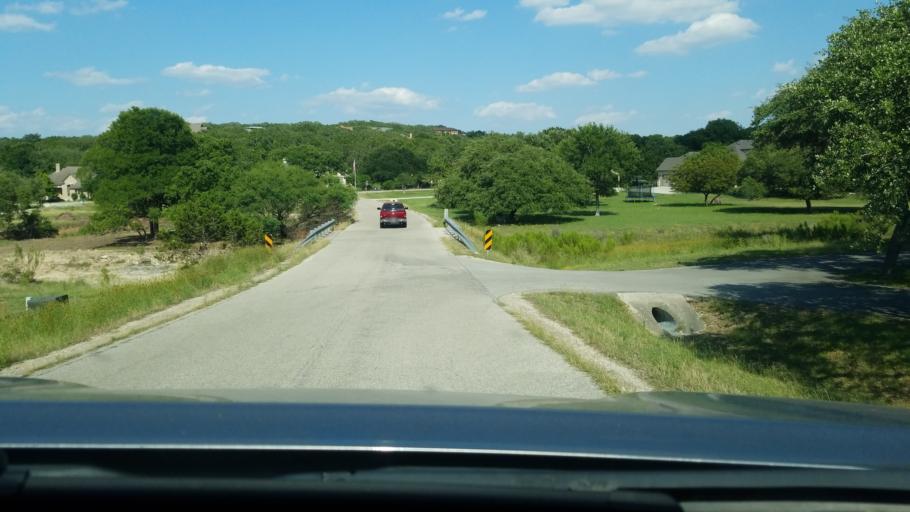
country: US
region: Texas
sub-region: Comal County
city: Bulverde
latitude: 29.8251
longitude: -98.4015
